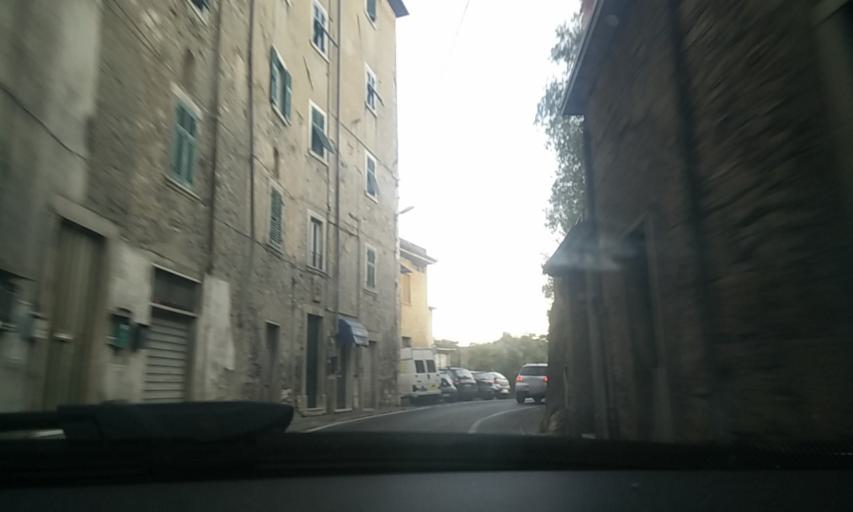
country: IT
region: Tuscany
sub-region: Provincia di Massa-Carrara
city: Carrara
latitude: 44.0783
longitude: 10.0950
